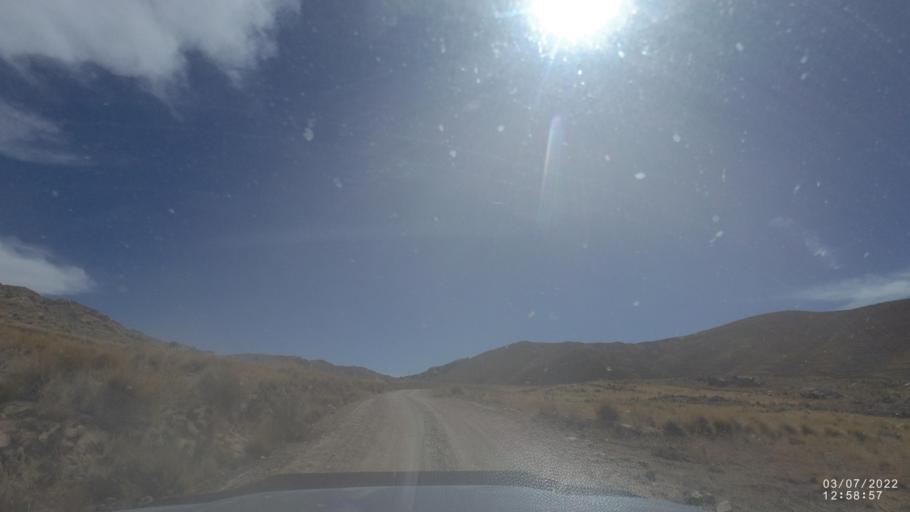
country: BO
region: Cochabamba
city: Sipe Sipe
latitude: -17.7183
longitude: -66.6829
